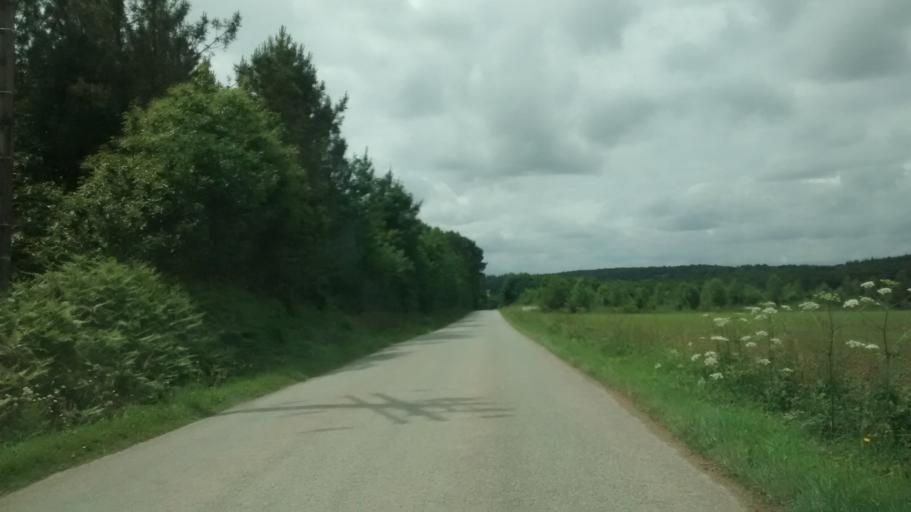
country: FR
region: Brittany
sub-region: Departement du Morbihan
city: Carentoir
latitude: 47.8219
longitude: -2.1552
